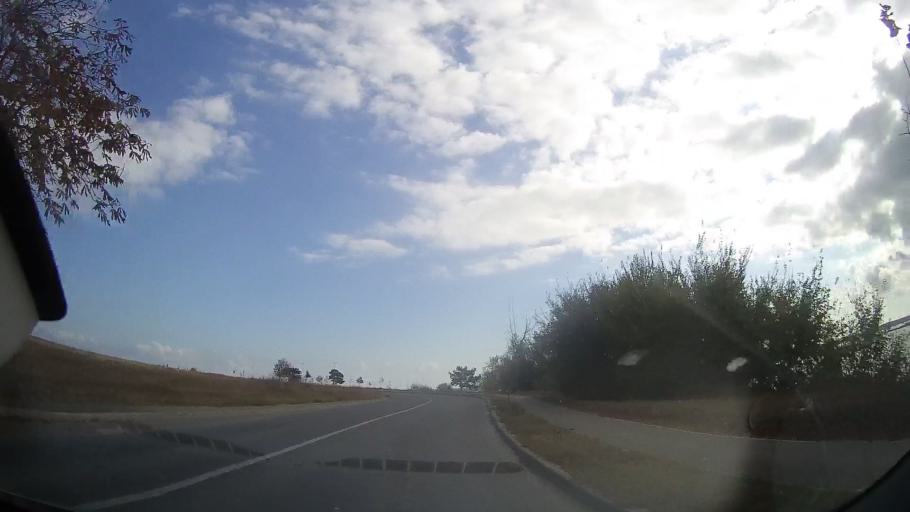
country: RO
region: Constanta
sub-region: Oras Techirghiol
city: Techirghiol
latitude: 44.0576
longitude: 28.6110
